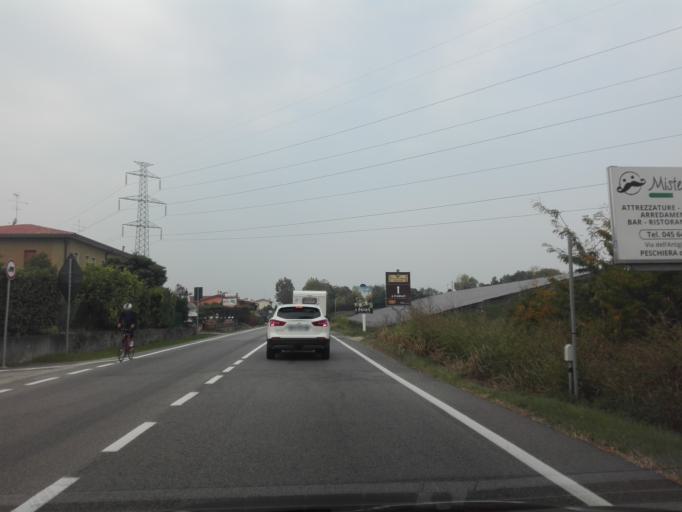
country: IT
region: Veneto
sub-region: Provincia di Verona
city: Castelnuovo del Garda
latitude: 45.4380
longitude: 10.7497
